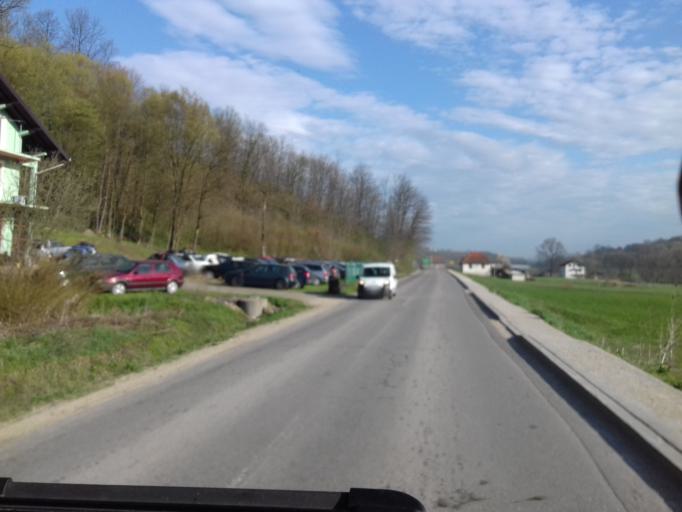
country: BA
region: Federation of Bosnia and Herzegovina
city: Tesanjka
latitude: 44.6445
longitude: 18.0193
